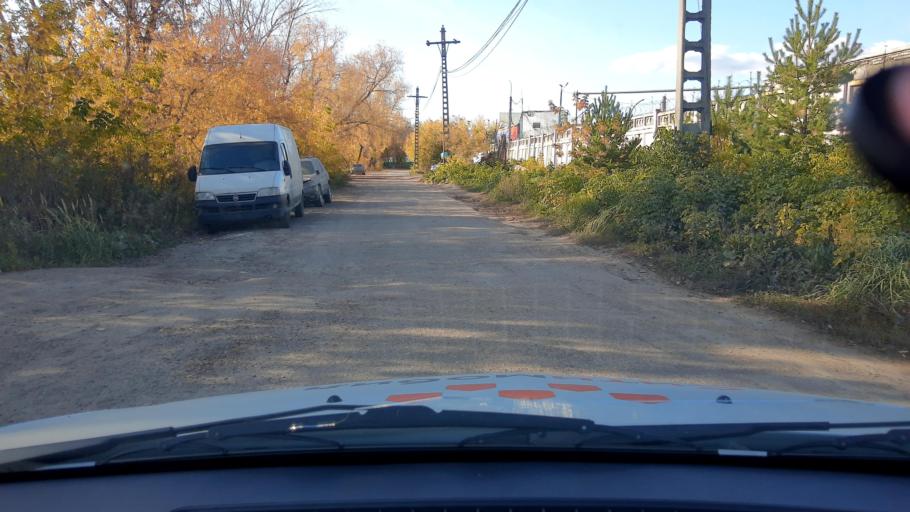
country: RU
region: Bashkortostan
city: Ufa
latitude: 54.7955
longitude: 56.0916
